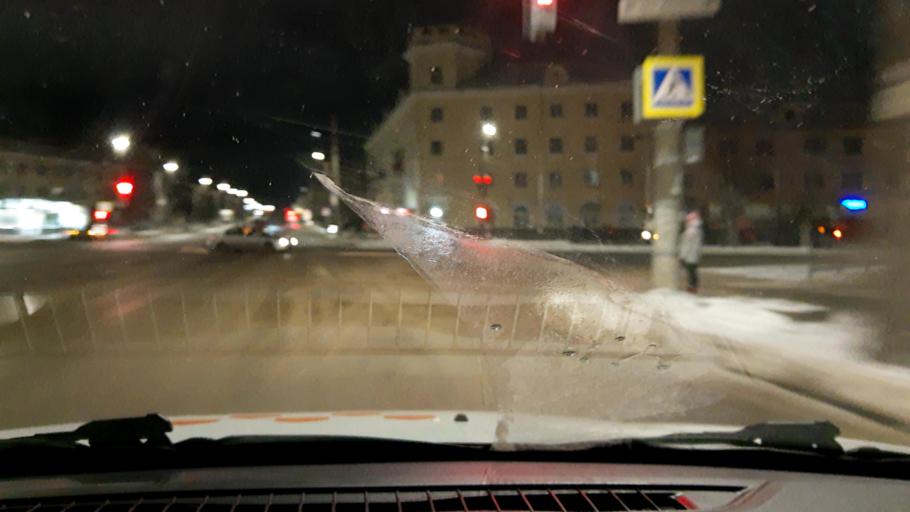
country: RU
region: Nizjnij Novgorod
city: Dzerzhinsk
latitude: 56.2392
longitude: 43.4847
